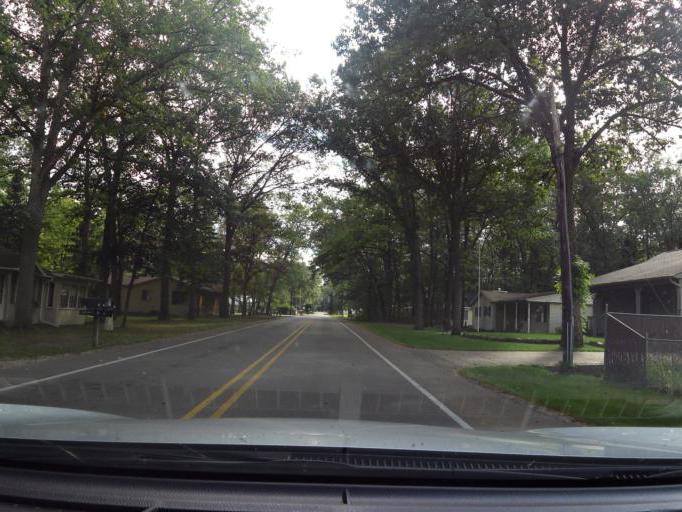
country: US
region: Michigan
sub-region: Roscommon County
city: Prudenville
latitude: 44.3023
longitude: -84.7029
